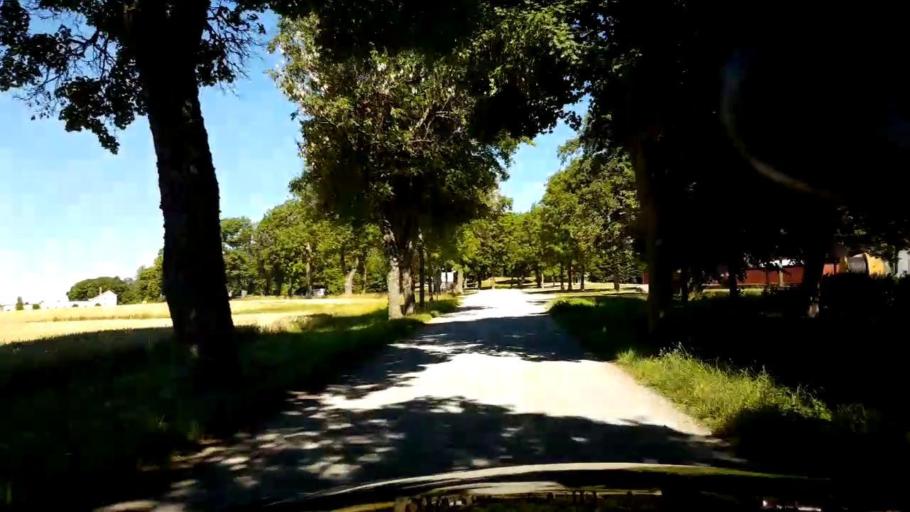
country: SE
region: Stockholm
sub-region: Sigtuna Kommun
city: Sigtuna
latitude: 59.6050
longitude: 17.6457
